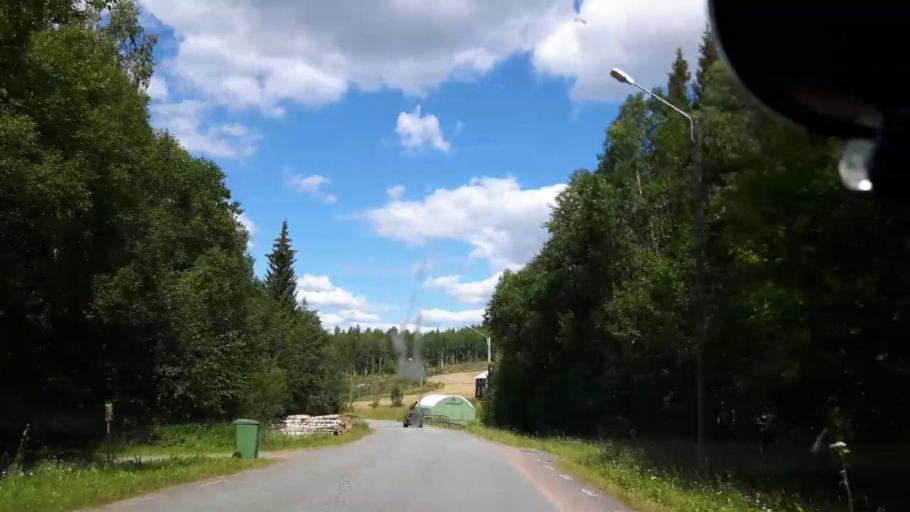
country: SE
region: Jaemtland
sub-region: Ragunda Kommun
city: Hammarstrand
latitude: 62.9414
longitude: 16.6922
